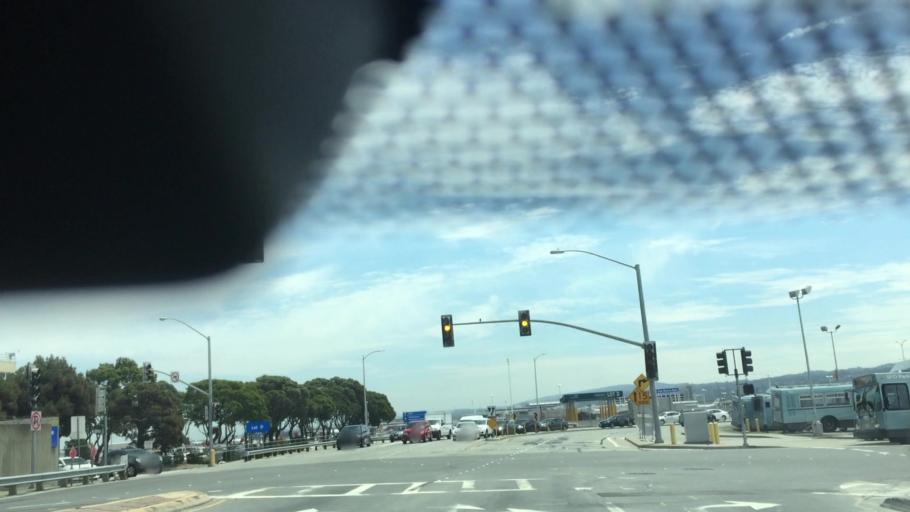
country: US
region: California
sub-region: San Mateo County
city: San Bruno
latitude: 37.6336
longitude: -122.3981
